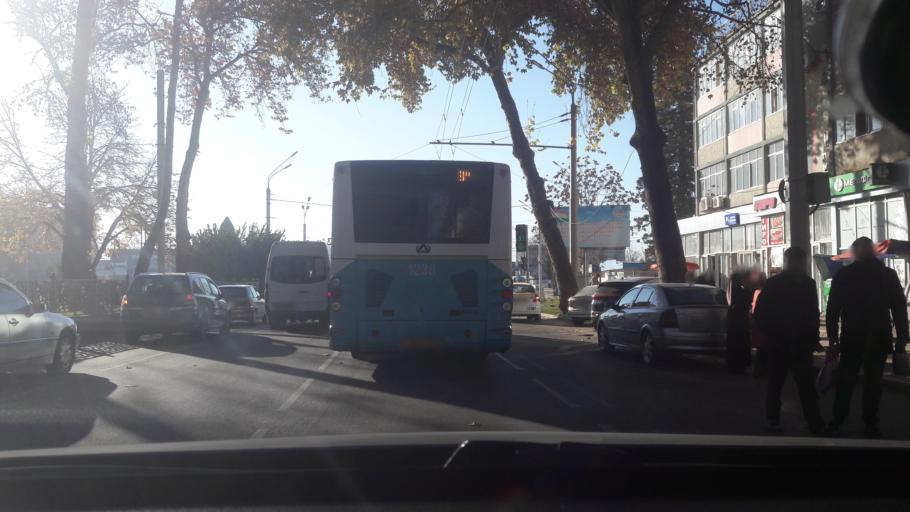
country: TJ
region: Dushanbe
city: Dushanbe
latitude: 38.5589
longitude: 68.7993
